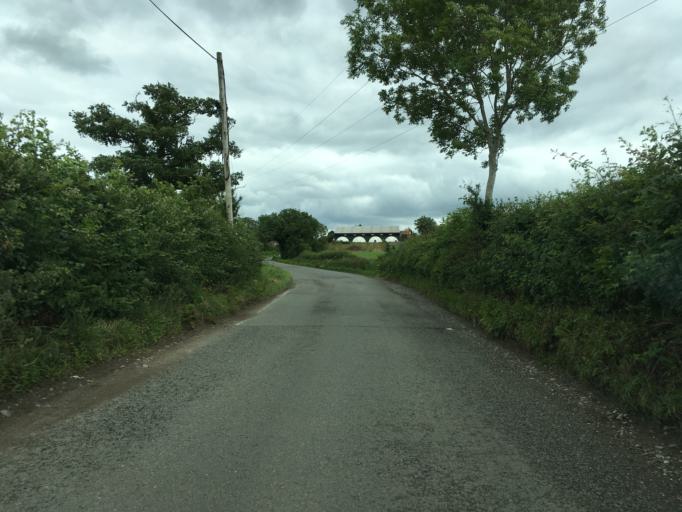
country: GB
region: England
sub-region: Gloucestershire
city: Cinderford
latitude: 51.7873
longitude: -2.4006
